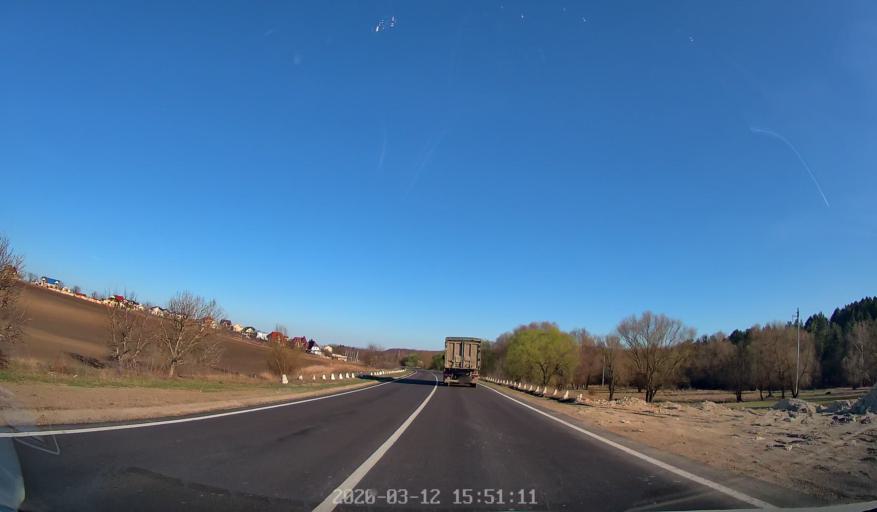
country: MD
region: Chisinau
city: Ciorescu
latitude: 47.0683
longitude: 28.9641
